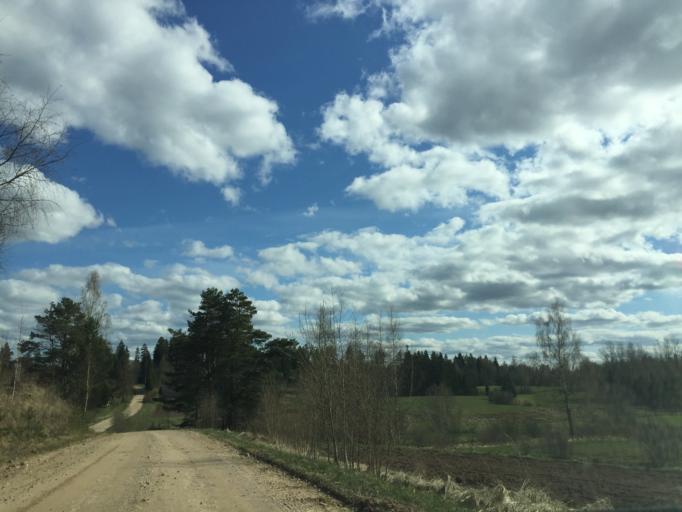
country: LV
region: Rezekne
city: Rezekne
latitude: 56.6595
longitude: 27.2708
